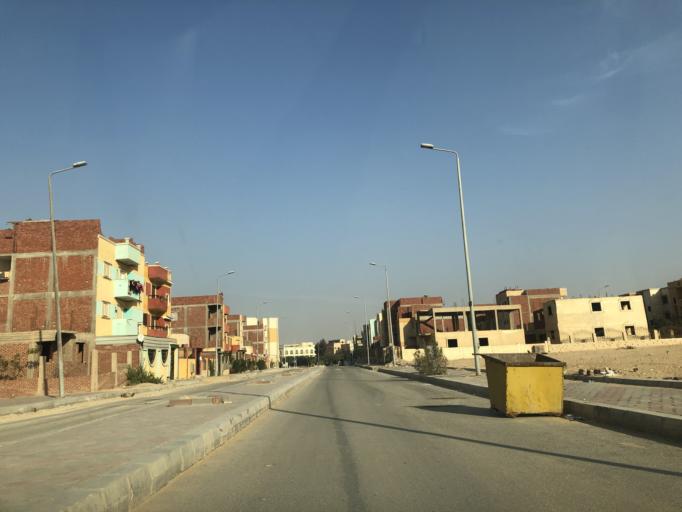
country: EG
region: Al Jizah
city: Madinat Sittah Uktubar
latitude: 29.9061
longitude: 30.9305
